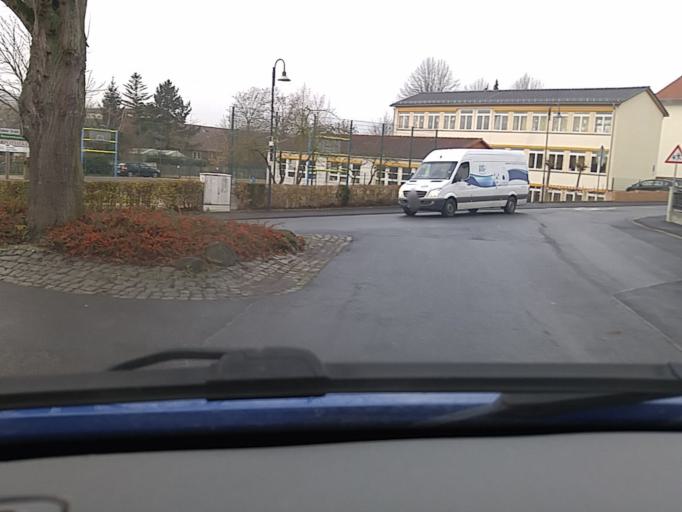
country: DE
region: Hesse
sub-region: Regierungsbezirk Darmstadt
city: Rockenberg
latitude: 50.3982
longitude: 8.7508
